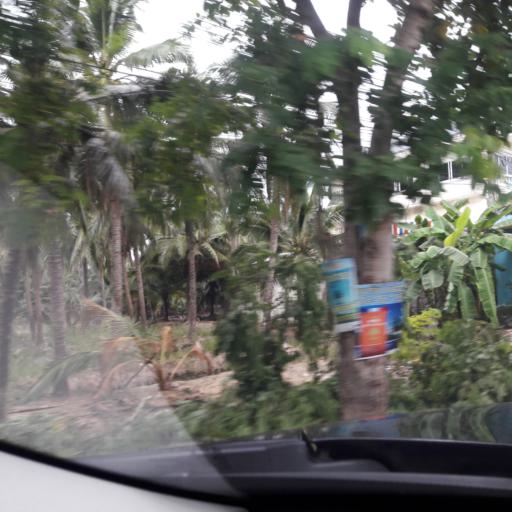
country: TH
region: Ratchaburi
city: Damnoen Saduak
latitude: 13.5750
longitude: 99.9377
